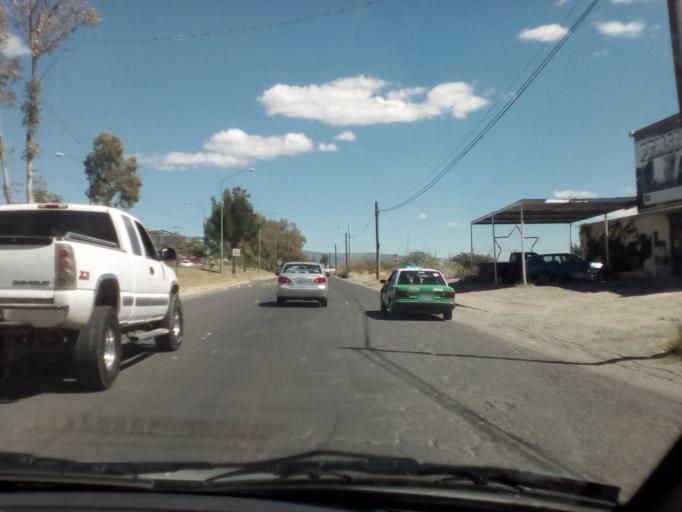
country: MX
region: Guanajuato
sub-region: Leon
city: La Ermita
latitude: 21.1436
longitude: -101.7172
